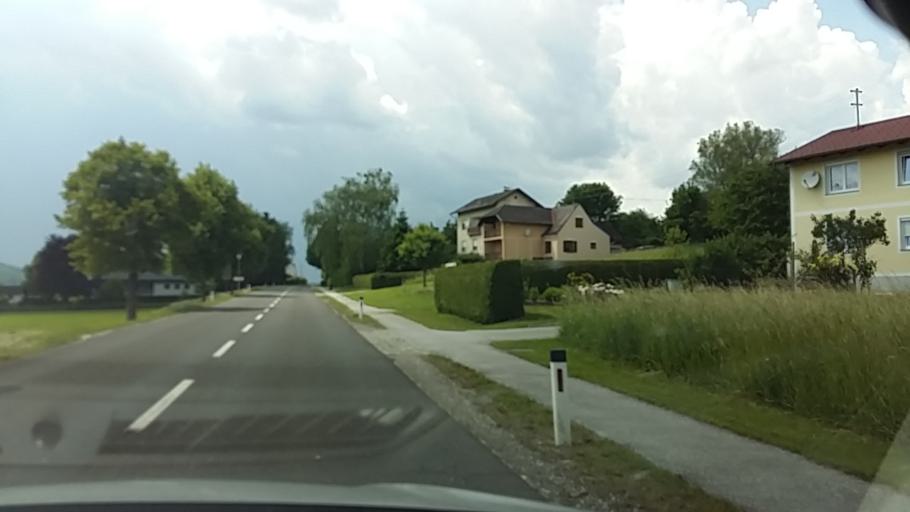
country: AT
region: Styria
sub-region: Politischer Bezirk Hartberg-Fuerstenfeld
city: Soechau
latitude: 47.0334
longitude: 16.0100
